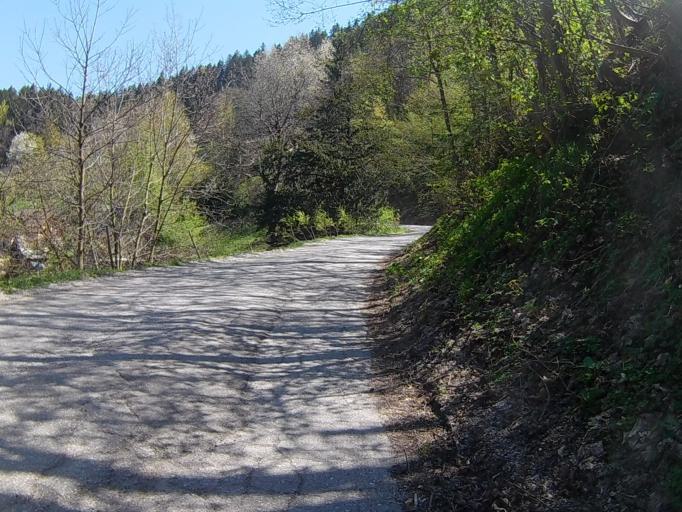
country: SI
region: Ruse
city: Ruse
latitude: 46.5222
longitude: 15.5186
